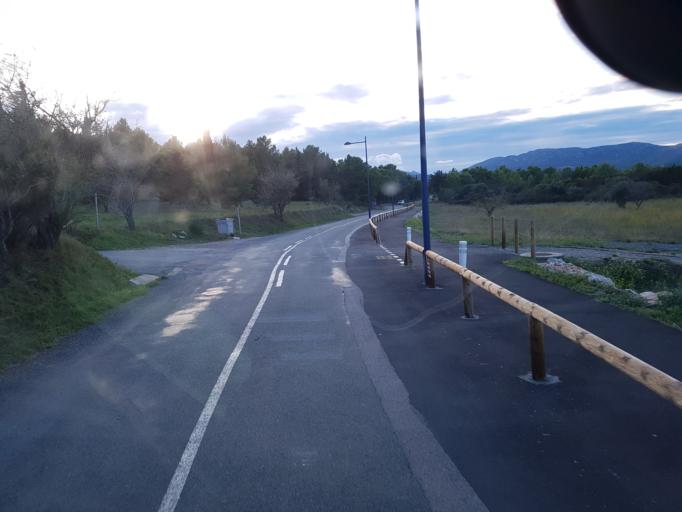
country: FR
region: Languedoc-Roussillon
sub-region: Departement de l'Aude
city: Leucate
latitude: 42.9337
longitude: 3.0221
